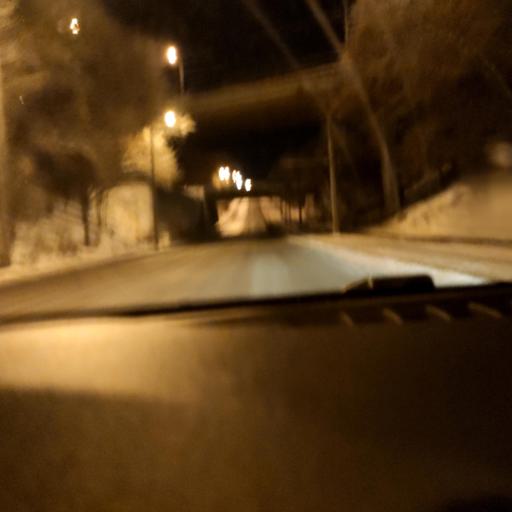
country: RU
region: Samara
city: Smyshlyayevka
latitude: 53.2232
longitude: 50.2821
